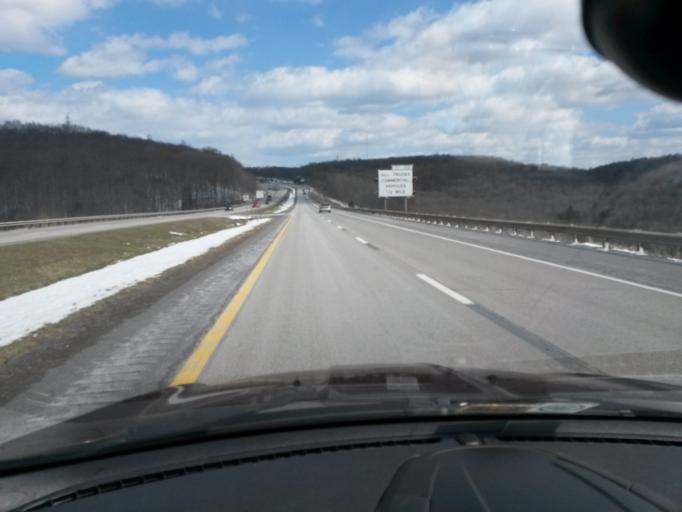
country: US
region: West Virginia
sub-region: Raleigh County
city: Shady Spring
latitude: 37.7676
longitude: -80.9973
